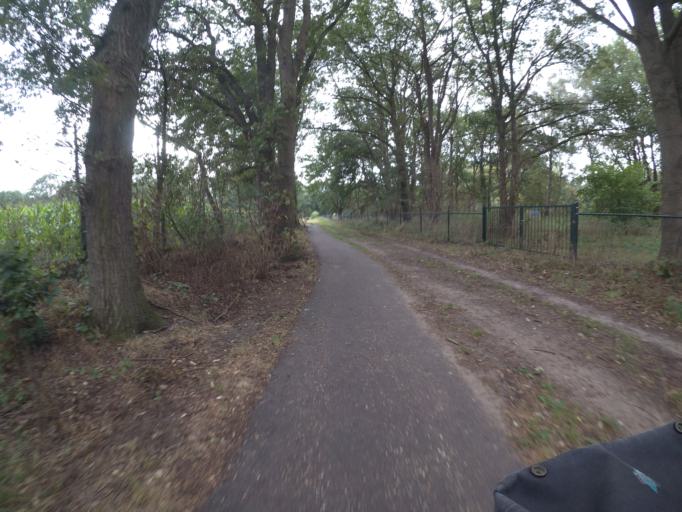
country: NL
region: North Brabant
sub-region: Gemeente Maasdonk
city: Geffen
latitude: 51.7366
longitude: 5.4931
